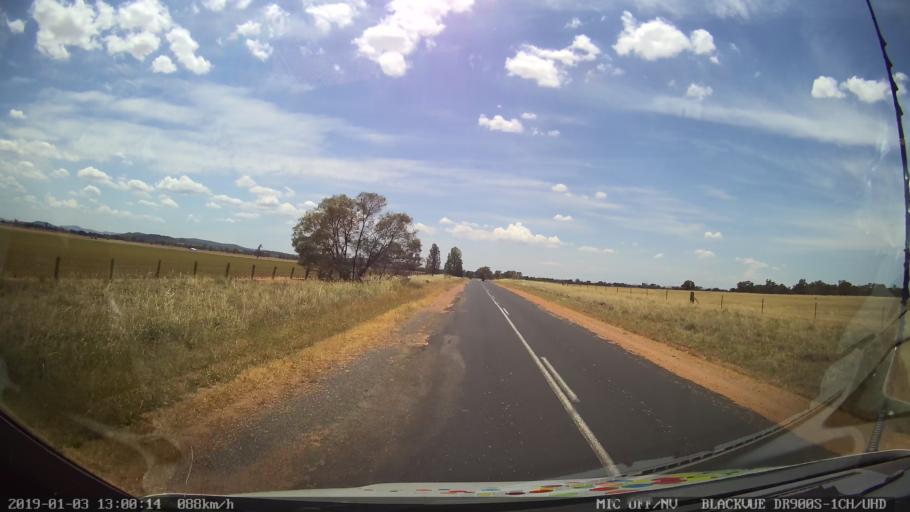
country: AU
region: New South Wales
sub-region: Cabonne
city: Canowindra
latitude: -33.6320
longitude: 148.4006
